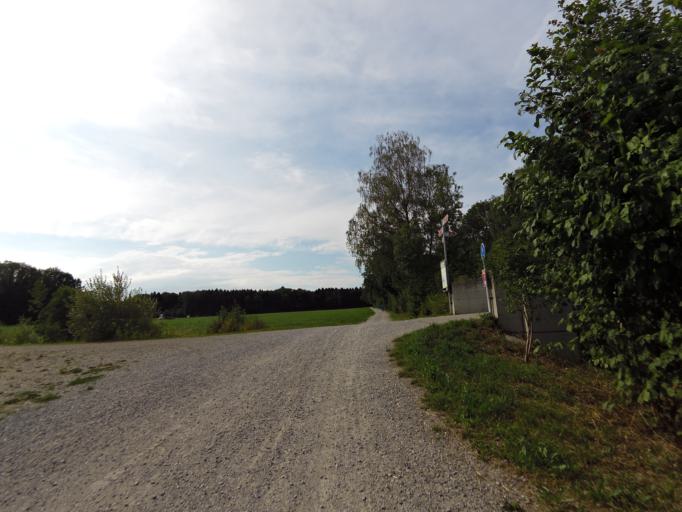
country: CH
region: Zurich
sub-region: Bezirk Buelach
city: Glattbrugg
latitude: 47.4378
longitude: 8.5573
